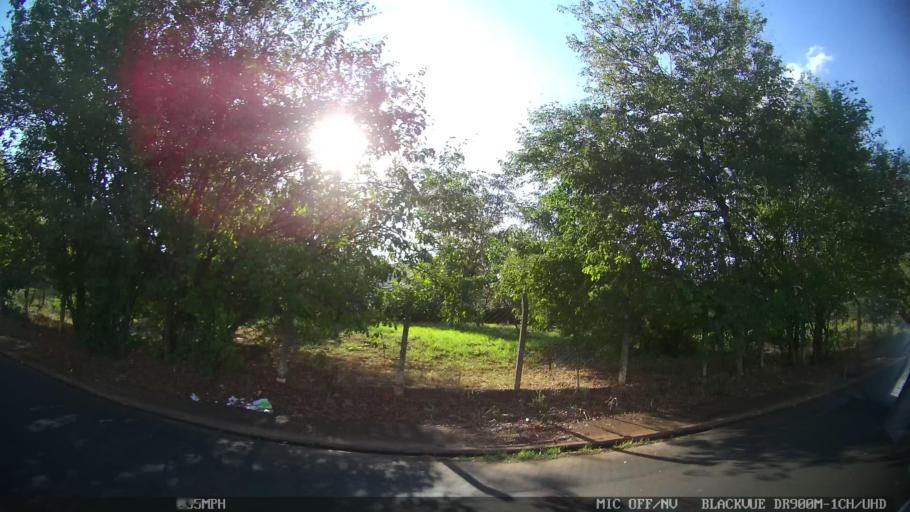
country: BR
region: Sao Paulo
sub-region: Ribeirao Preto
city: Ribeirao Preto
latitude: -21.2070
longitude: -47.7773
